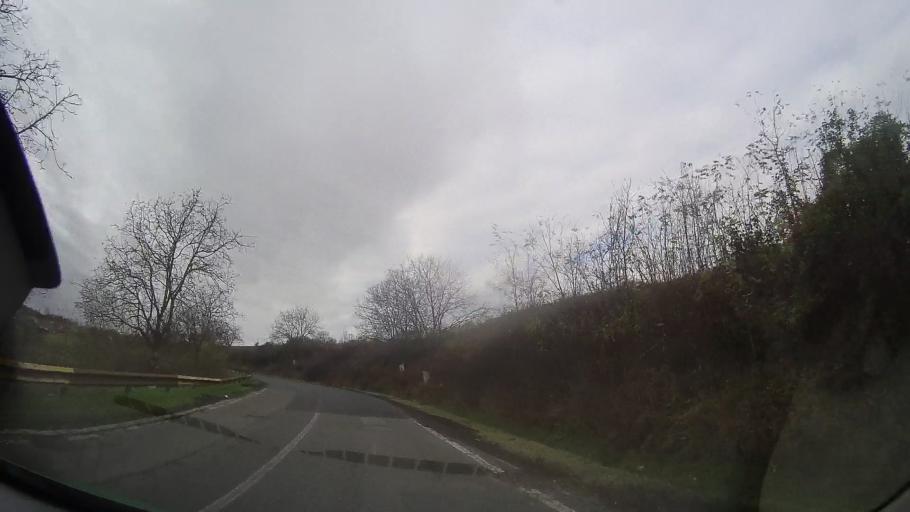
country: RO
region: Bistrita-Nasaud
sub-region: Comuna Silvasu de Campie
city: Silvasu de Campie
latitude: 46.7775
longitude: 24.3216
